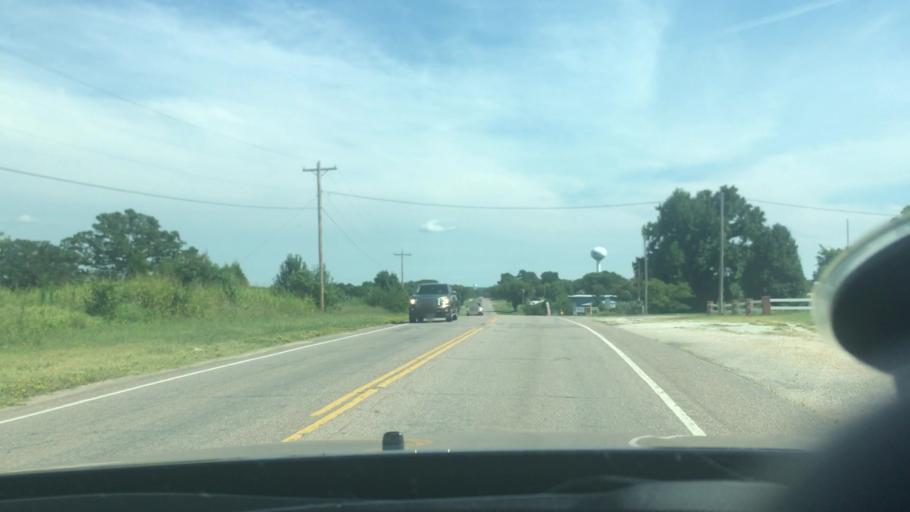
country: US
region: Oklahoma
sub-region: Seminole County
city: Seminole
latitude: 35.2420
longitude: -96.6973
